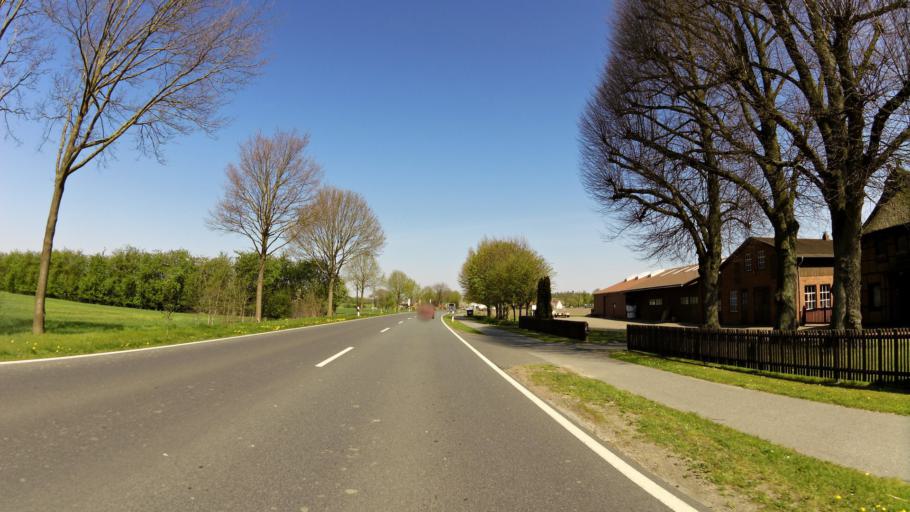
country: DE
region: Lower Saxony
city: Ganderkesee
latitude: 53.0821
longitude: 8.5254
